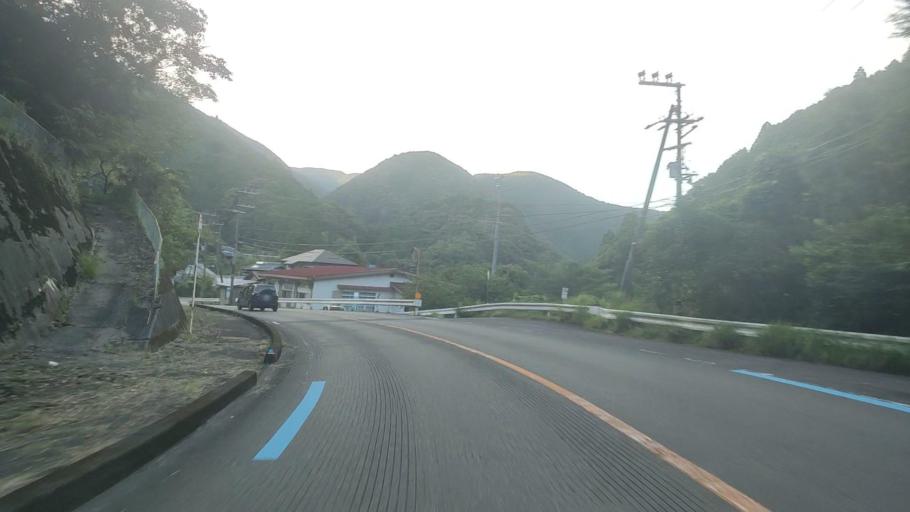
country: JP
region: Wakayama
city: Tanabe
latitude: 33.8116
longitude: 135.5498
